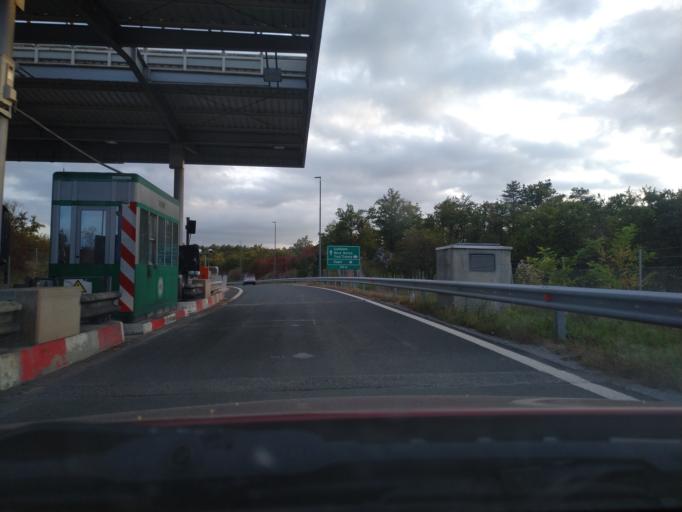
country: SI
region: Divaca
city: Divaca
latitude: 45.6702
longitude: 13.9666
